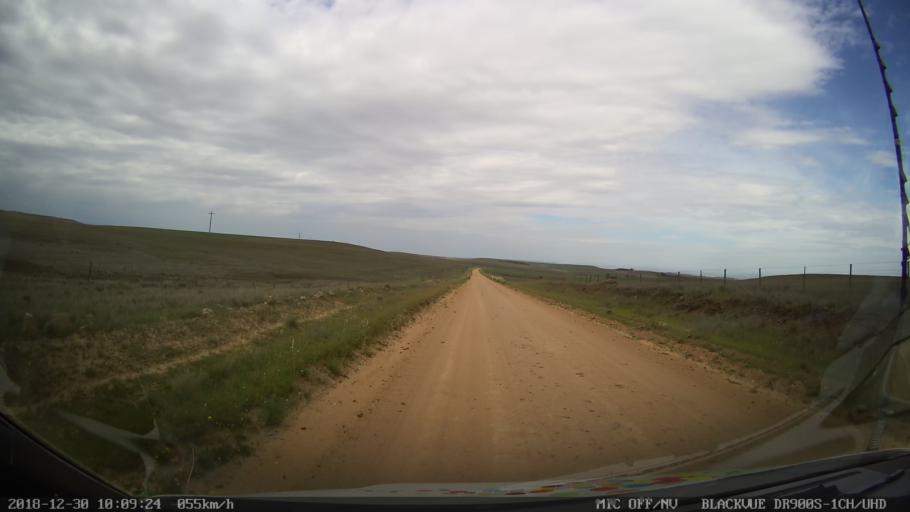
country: AU
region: New South Wales
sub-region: Cooma-Monaro
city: Cooma
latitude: -36.5482
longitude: 149.1058
